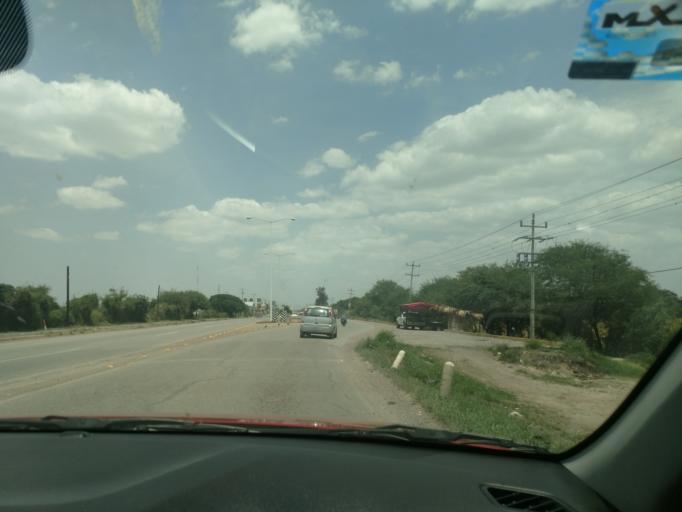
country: MX
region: San Luis Potosi
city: Ciudad Fernandez
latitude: 21.9387
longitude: -100.0343
